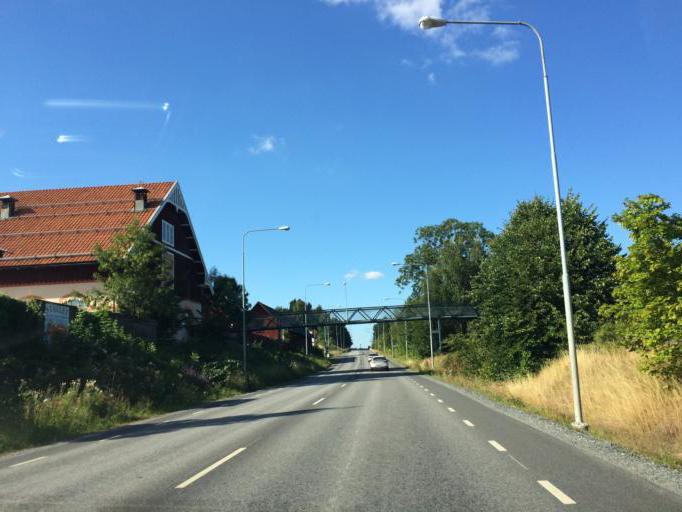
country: SE
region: Stockholm
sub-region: Sollentuna Kommun
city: Sollentuna
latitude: 59.4652
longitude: 17.9221
